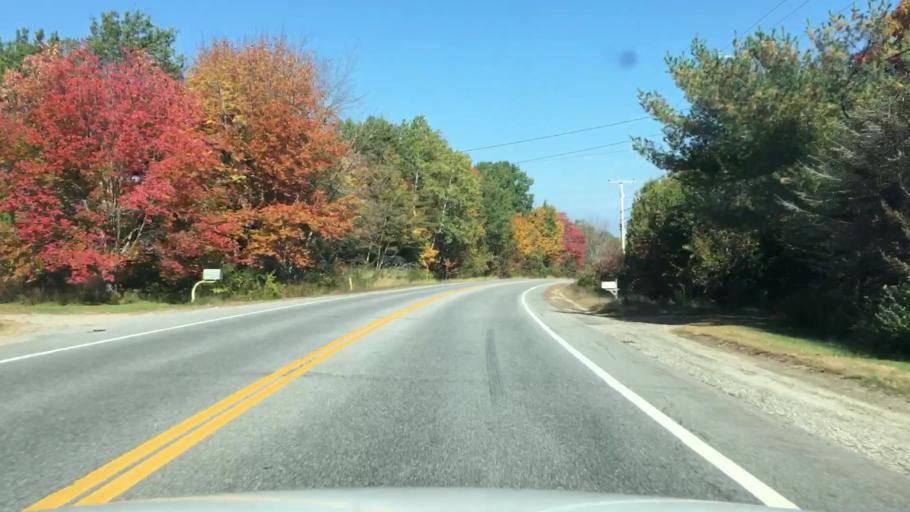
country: US
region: Maine
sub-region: Sagadahoc County
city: Topsham
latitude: 43.9787
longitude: -69.9609
